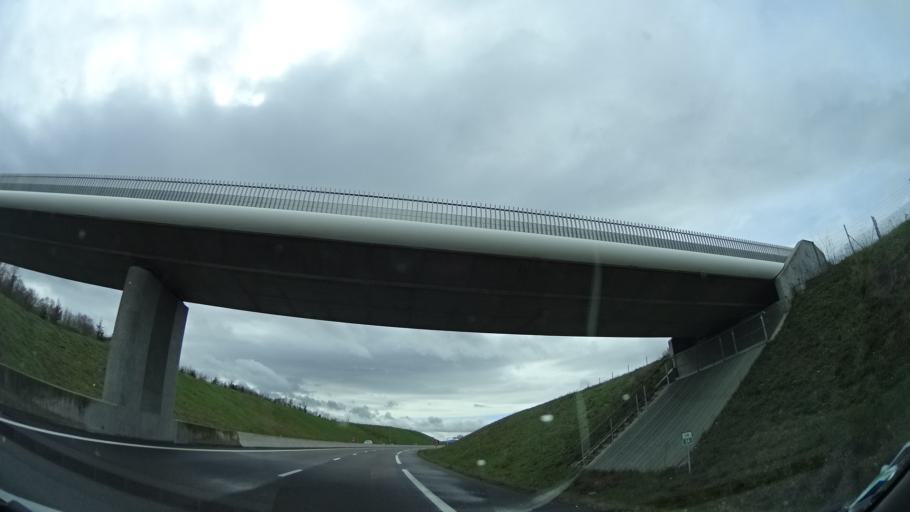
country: FR
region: Rhone-Alpes
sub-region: Departement du Rhone
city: Lentilly
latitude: 45.8481
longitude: 4.6465
